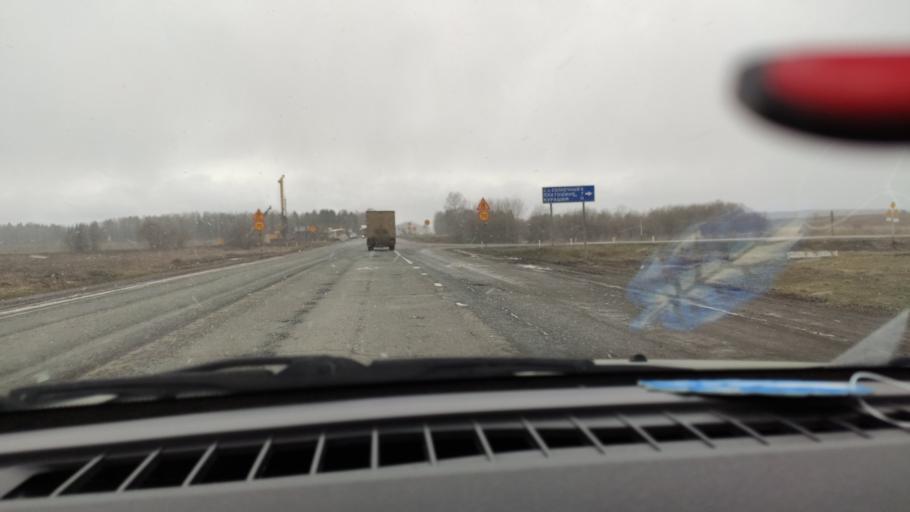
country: RU
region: Perm
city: Kukushtan
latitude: 57.6099
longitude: 56.5034
